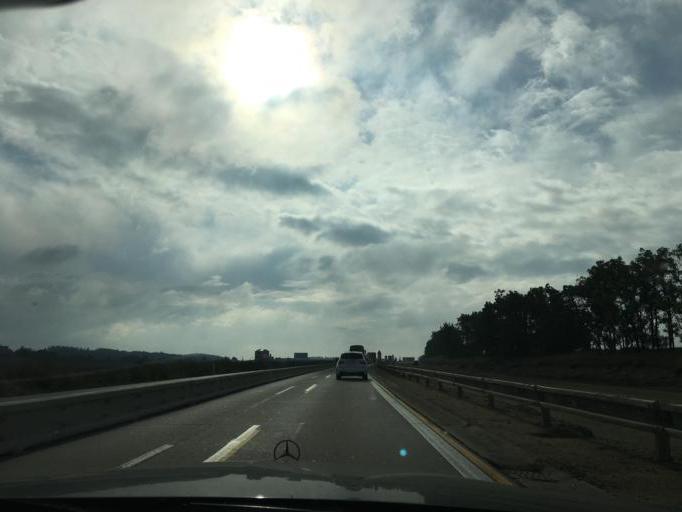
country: CZ
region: Vysocina
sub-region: Okres Zd'ar nad Sazavou
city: Velke Mezirici
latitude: 49.3290
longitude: 16.0750
